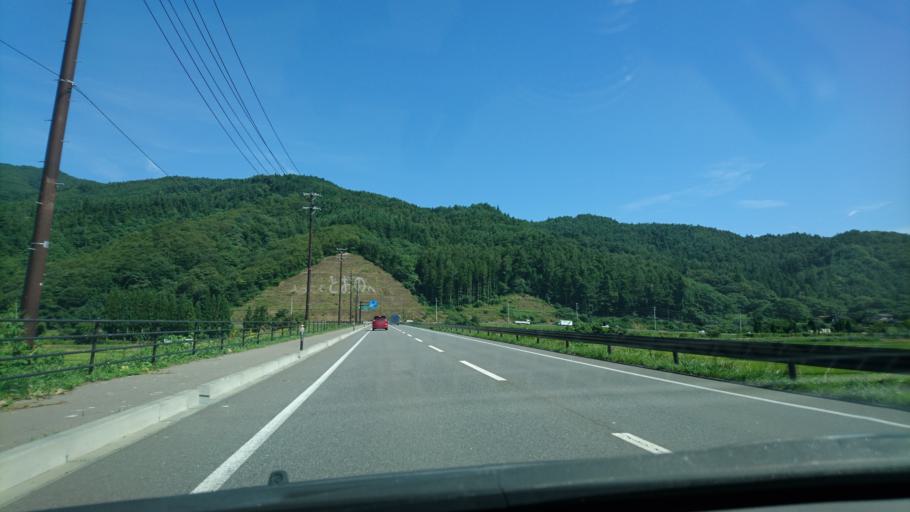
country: JP
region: Iwate
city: Tono
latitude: 39.3298
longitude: 141.5094
